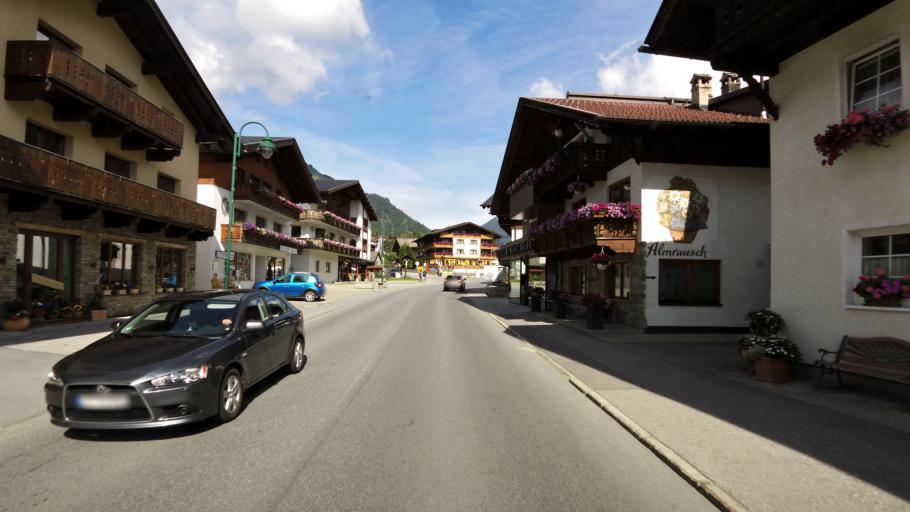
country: AT
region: Tyrol
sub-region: Politischer Bezirk Reutte
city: Lermoos
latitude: 47.4017
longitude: 10.8815
